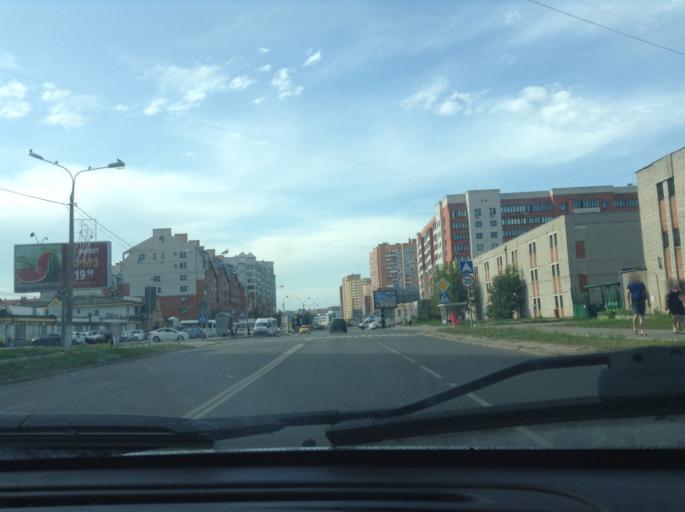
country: RU
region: Moskovskaya
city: Bykovo
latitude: 55.5976
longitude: 38.0909
